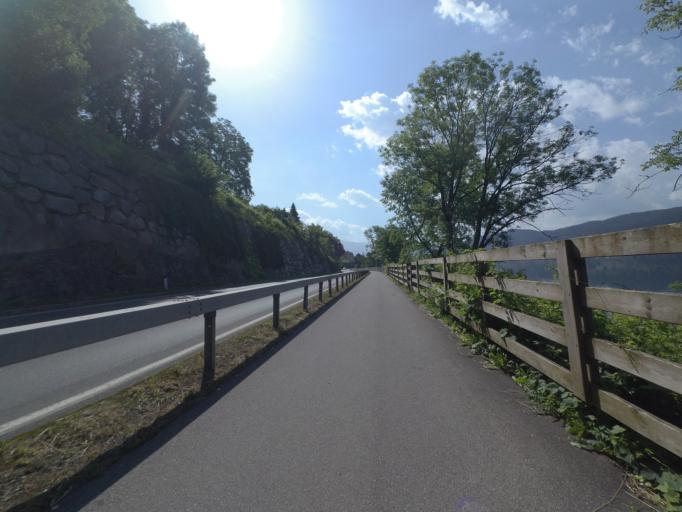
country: AT
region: Carinthia
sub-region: Politischer Bezirk Spittal an der Drau
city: Millstatt
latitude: 46.8083
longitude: 13.5604
